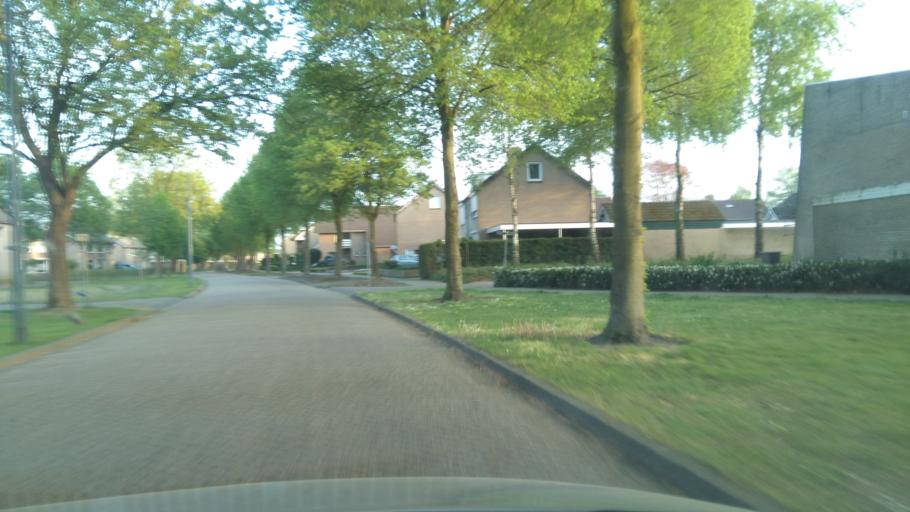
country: NL
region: North Brabant
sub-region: Gemeente Baarle-Nassau
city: Baarle-Nassau
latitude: 51.4496
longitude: 4.9285
